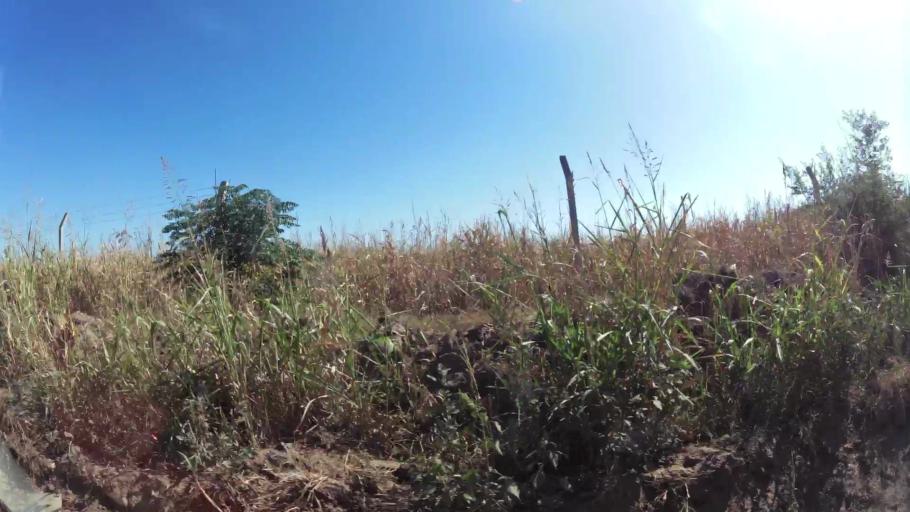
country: AR
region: Cordoba
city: Villa Allende
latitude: -31.3206
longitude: -64.2456
